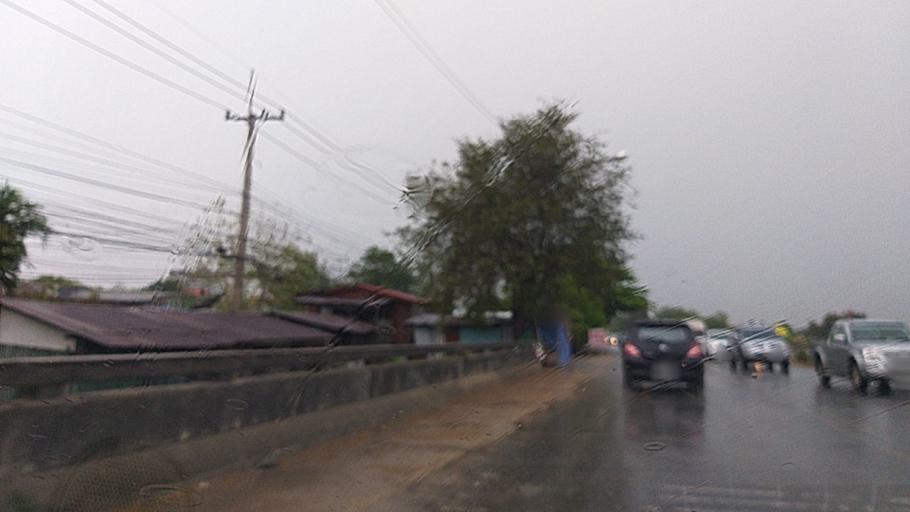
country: TH
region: Phra Nakhon Si Ayutthaya
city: Phra Nakhon Si Ayutthaya
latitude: 14.3447
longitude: 100.5847
